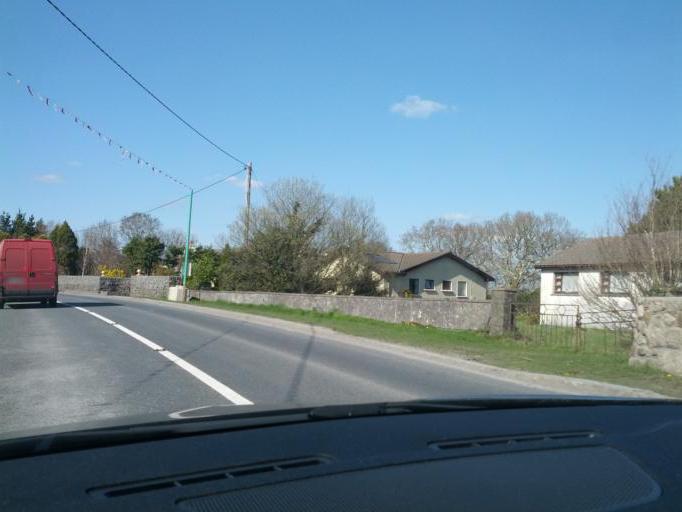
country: IE
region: Connaught
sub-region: County Galway
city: Moycullen
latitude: 53.3285
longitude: -9.1688
